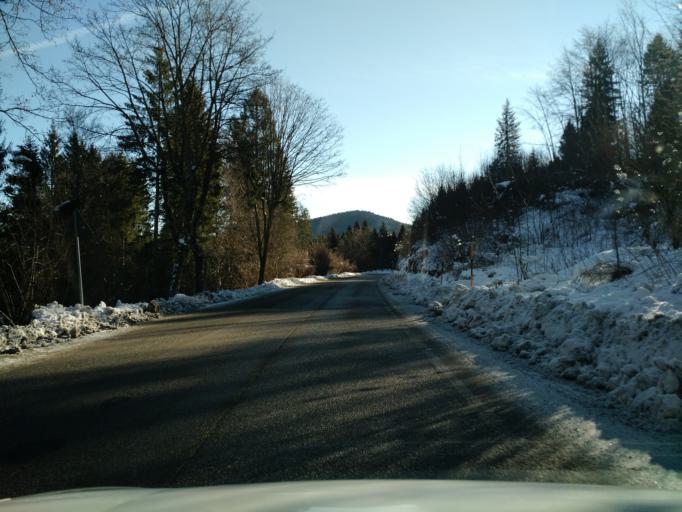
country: IT
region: Veneto
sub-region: Provincia di Vicenza
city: Canove di Roana
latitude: 45.8383
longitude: 11.4433
